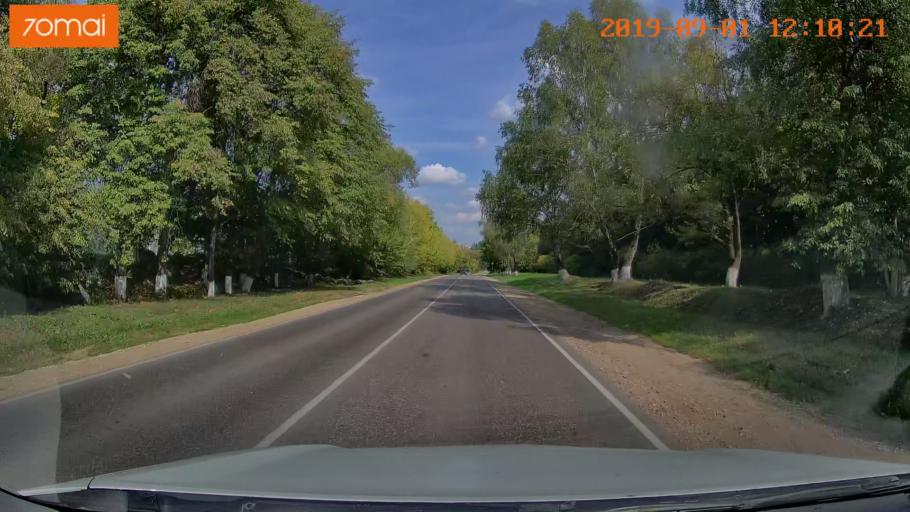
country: RU
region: Kaluga
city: Maloyaroslavets
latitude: 54.9907
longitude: 36.4321
